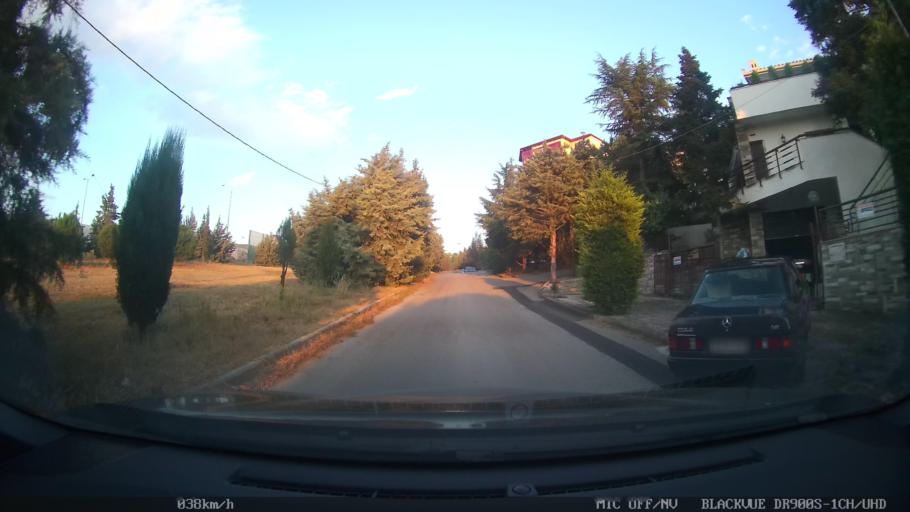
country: GR
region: Central Macedonia
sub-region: Nomos Thessalonikis
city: Pylaia
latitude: 40.6133
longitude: 22.9915
